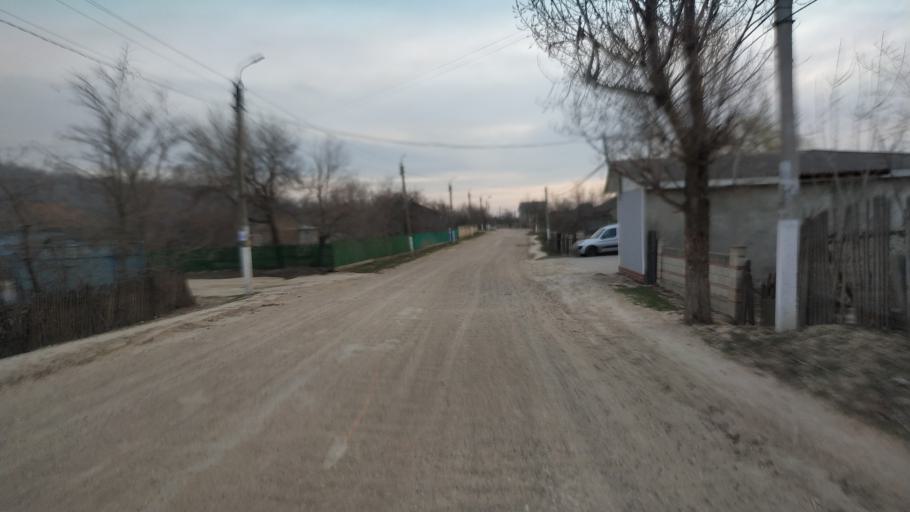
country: MD
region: Hincesti
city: Dancu
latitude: 46.7543
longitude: 28.2075
